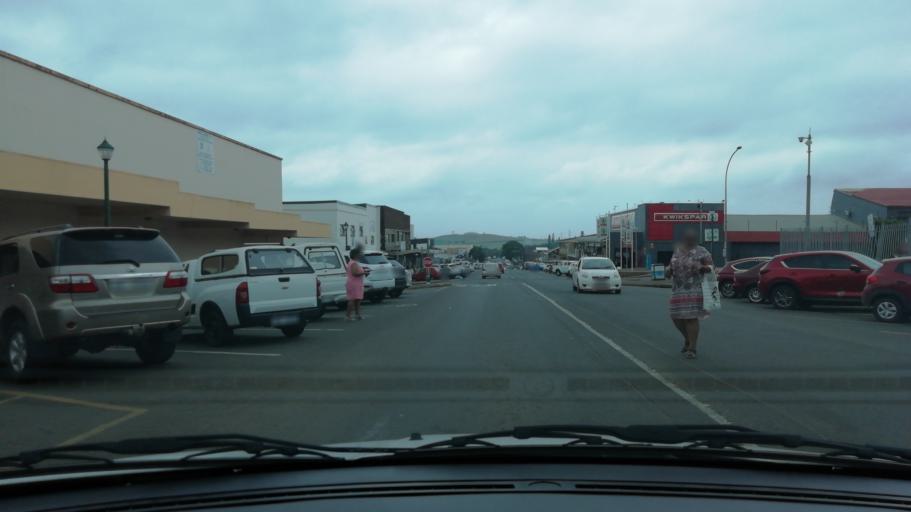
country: ZA
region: KwaZulu-Natal
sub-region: uThungulu District Municipality
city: Empangeni
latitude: -28.7429
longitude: 31.8919
